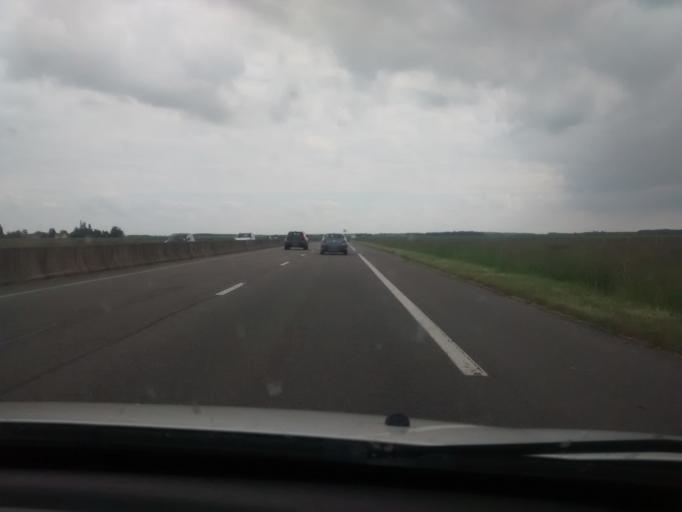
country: FR
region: Ile-de-France
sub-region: Departement des Yvelines
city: Sonchamp
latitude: 48.5898
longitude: 1.8319
